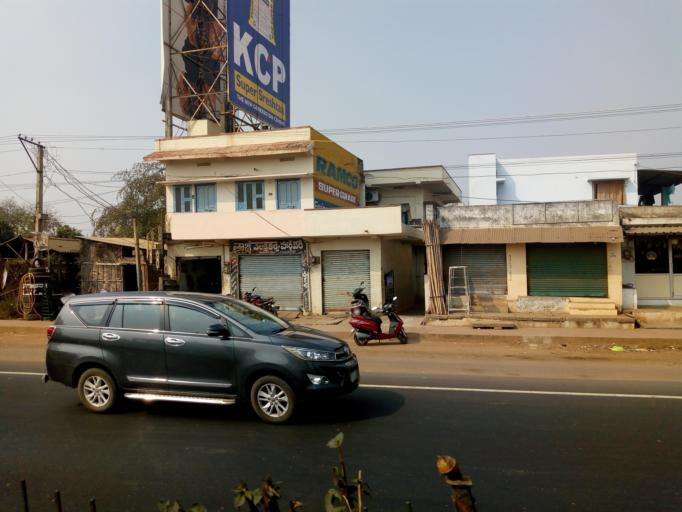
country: IN
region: Andhra Pradesh
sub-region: West Godavari
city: Eluru
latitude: 16.6339
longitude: 80.9628
